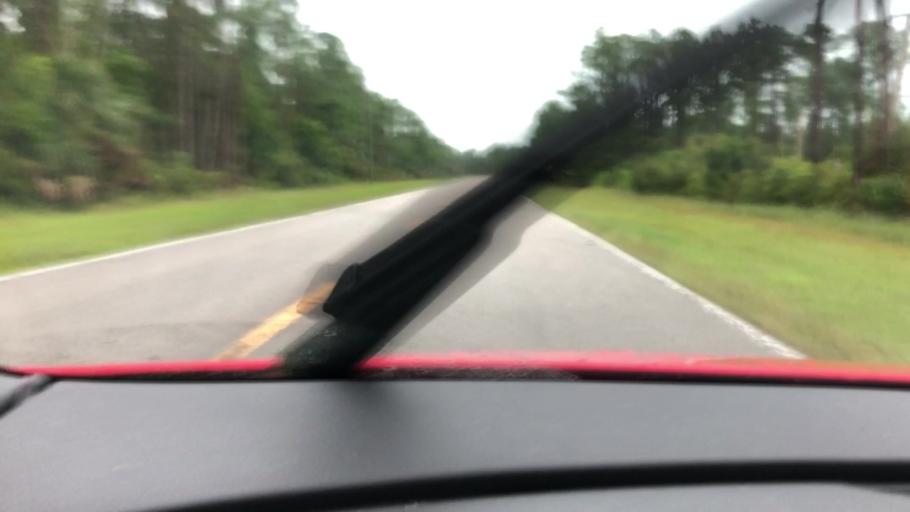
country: US
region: Florida
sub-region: Volusia County
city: Samsula-Spruce Creek
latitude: 29.0345
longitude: -81.0873
